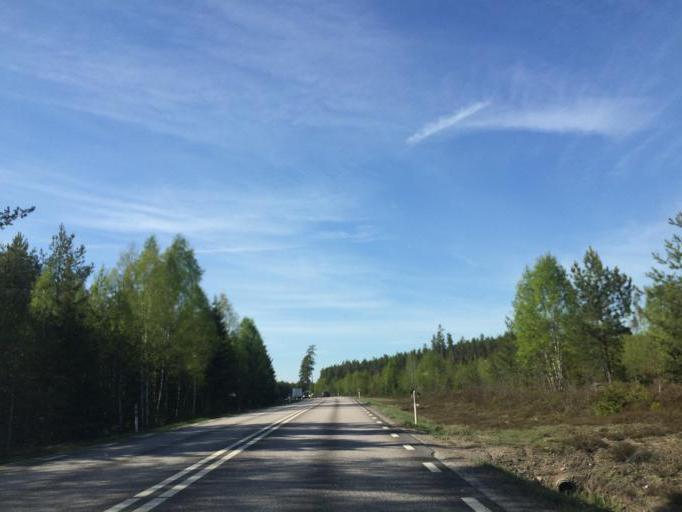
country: SE
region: Soedermanland
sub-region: Katrineholms Kommun
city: Katrineholm
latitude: 59.1165
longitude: 16.1633
